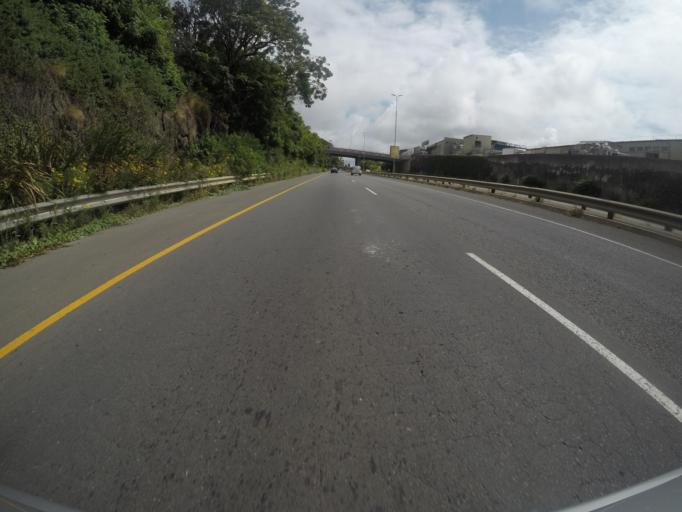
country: ZA
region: Eastern Cape
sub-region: Buffalo City Metropolitan Municipality
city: East London
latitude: -32.9866
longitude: 27.9192
